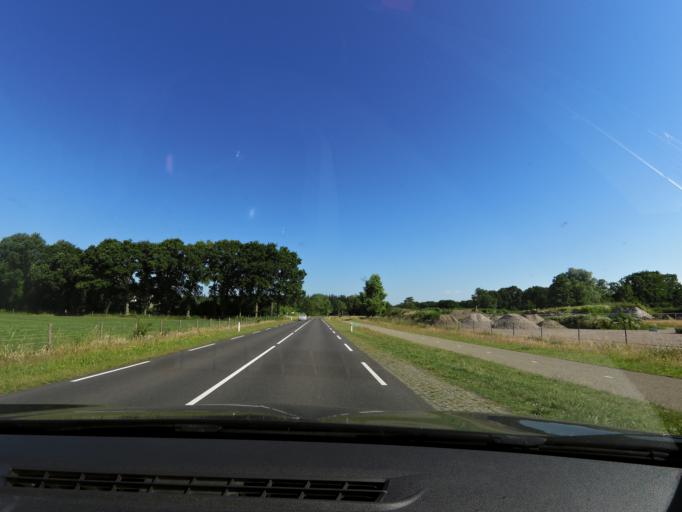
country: NL
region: Overijssel
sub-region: Gemeente Twenterand
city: Den Ham
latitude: 52.4013
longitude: 6.4422
